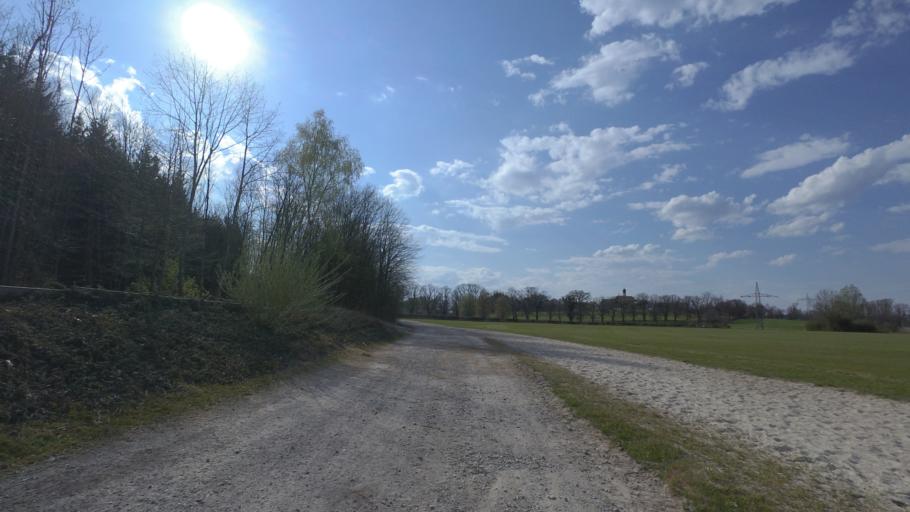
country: DE
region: Bavaria
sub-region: Upper Bavaria
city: Chieming
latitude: 47.9206
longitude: 12.5138
